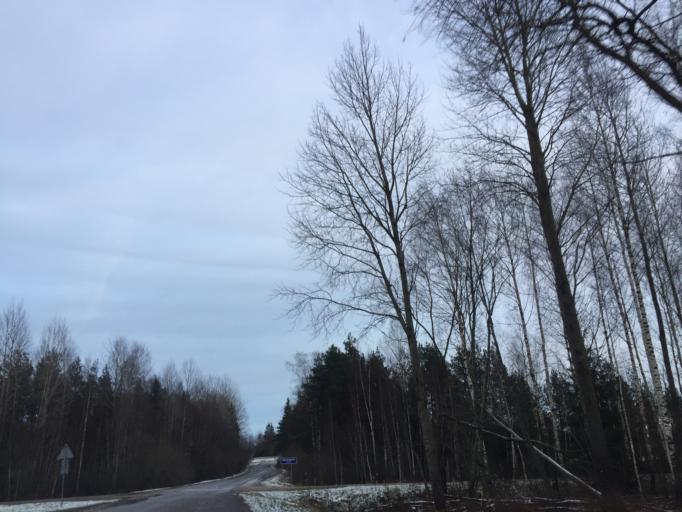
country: LV
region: Aloja
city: Aloja
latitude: 57.6151
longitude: 24.9024
